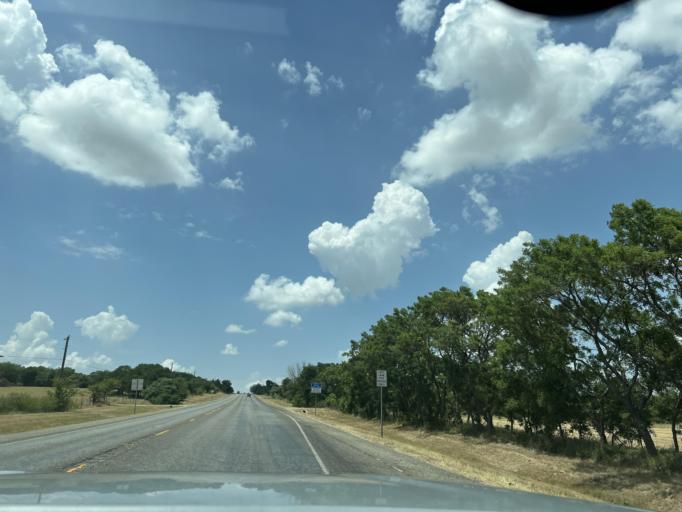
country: US
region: Texas
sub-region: Parker County
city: Springtown
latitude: 32.9378
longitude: -97.6980
